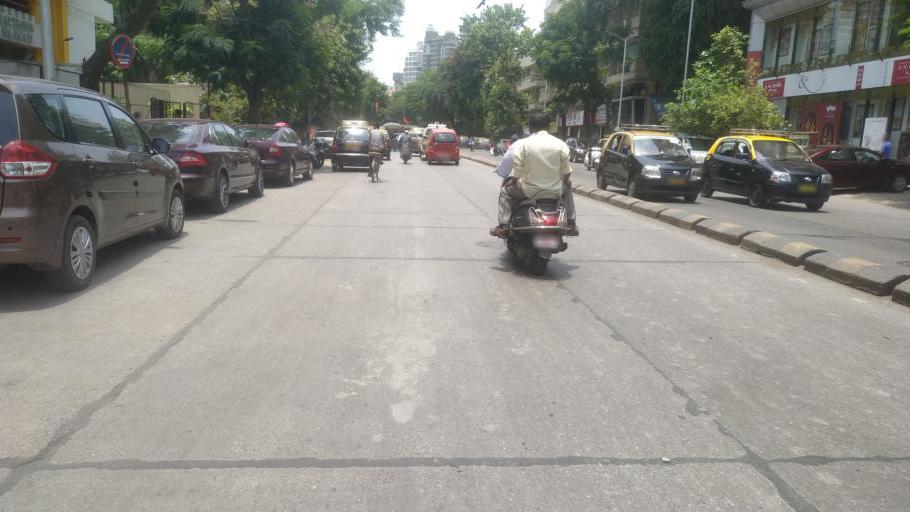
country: IN
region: Maharashtra
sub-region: Mumbai Suburban
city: Mumbai
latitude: 19.0145
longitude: 72.8311
